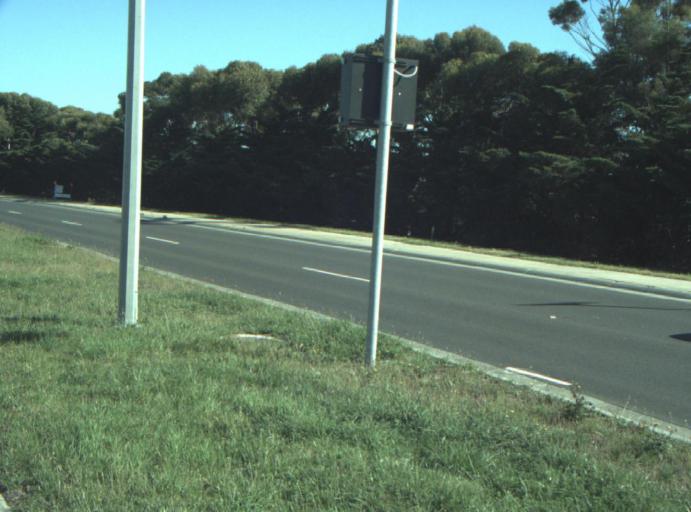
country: AU
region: Victoria
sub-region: Greater Geelong
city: Hamlyn Heights
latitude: -38.1087
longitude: 144.3239
